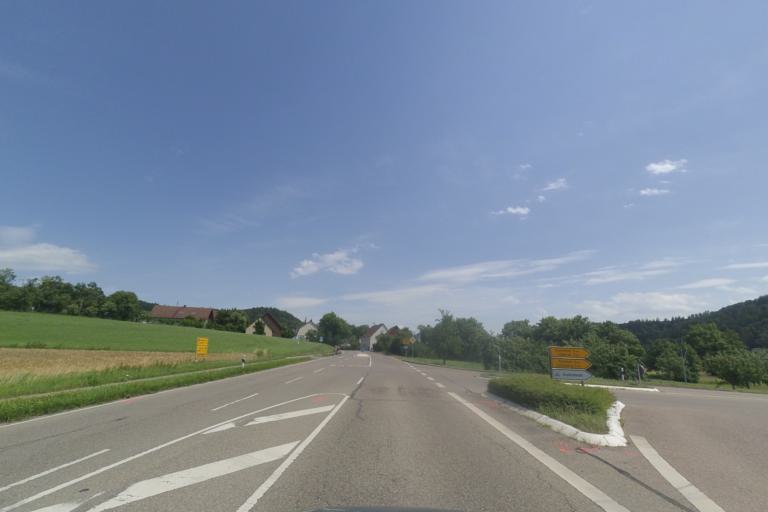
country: DE
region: Baden-Wuerttemberg
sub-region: Regierungsbezirk Stuttgart
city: Gaildorf
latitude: 48.9787
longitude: 9.7972
